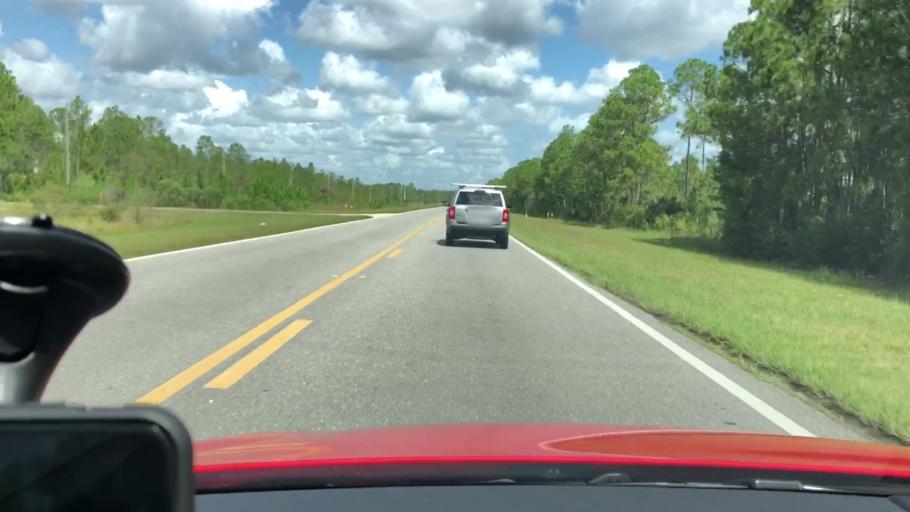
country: US
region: Florida
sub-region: Volusia County
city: Holly Hill
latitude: 29.2025
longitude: -81.1198
